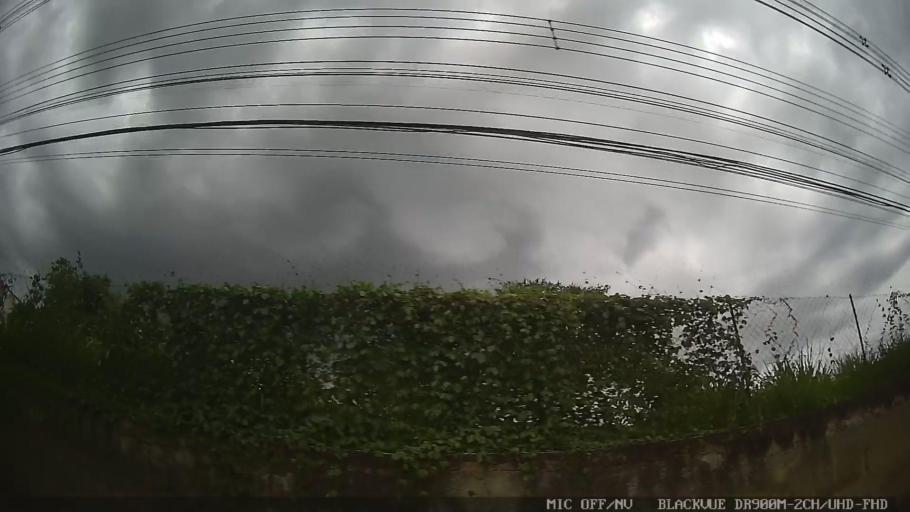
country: BR
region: Sao Paulo
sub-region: Amparo
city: Amparo
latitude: -22.7067
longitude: -46.7797
